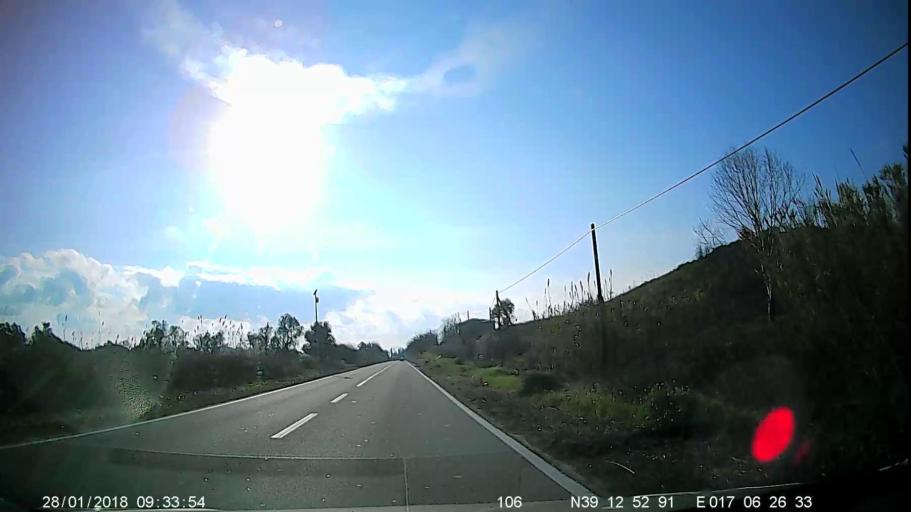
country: IT
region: Calabria
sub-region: Provincia di Crotone
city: Tronca
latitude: 39.2143
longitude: 17.1075
